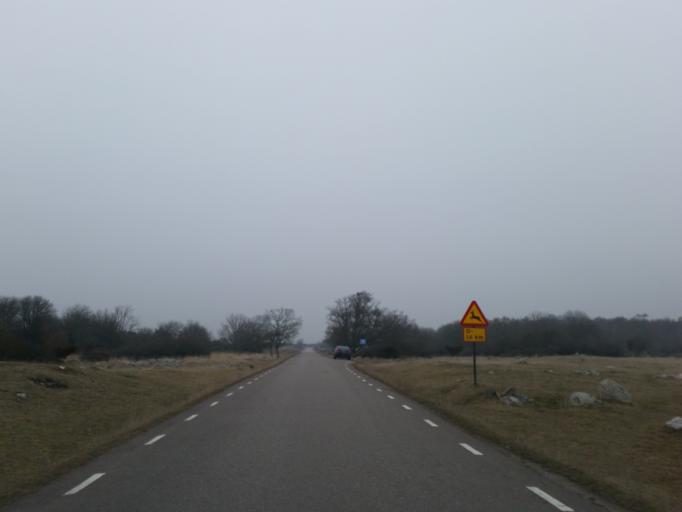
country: SE
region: Kalmar
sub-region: Morbylanga Kommun
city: Moerbylanga
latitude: 56.2112
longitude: 16.4068
